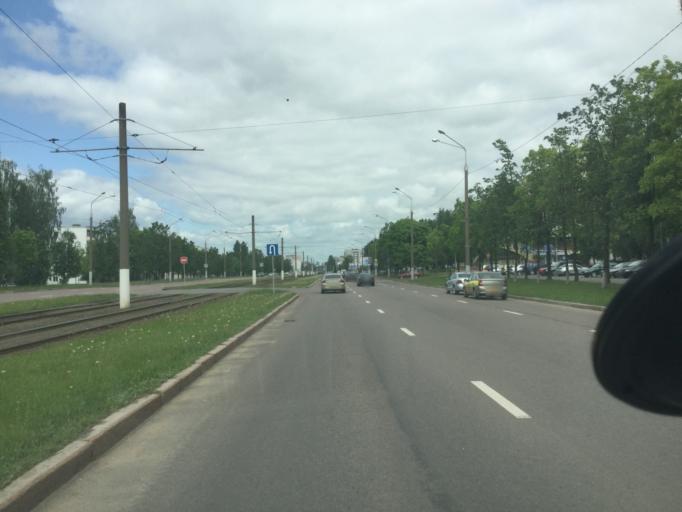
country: BY
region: Vitebsk
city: Vitebsk
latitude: 55.1794
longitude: 30.2292
